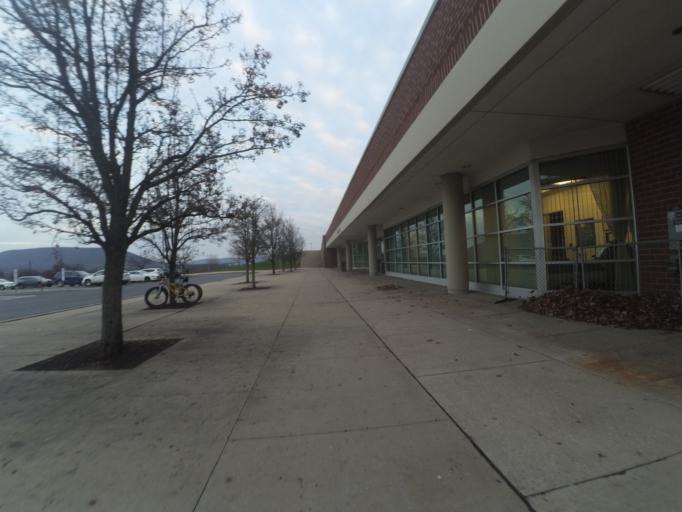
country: US
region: Pennsylvania
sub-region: Centre County
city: State College
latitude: 40.8094
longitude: -77.8554
